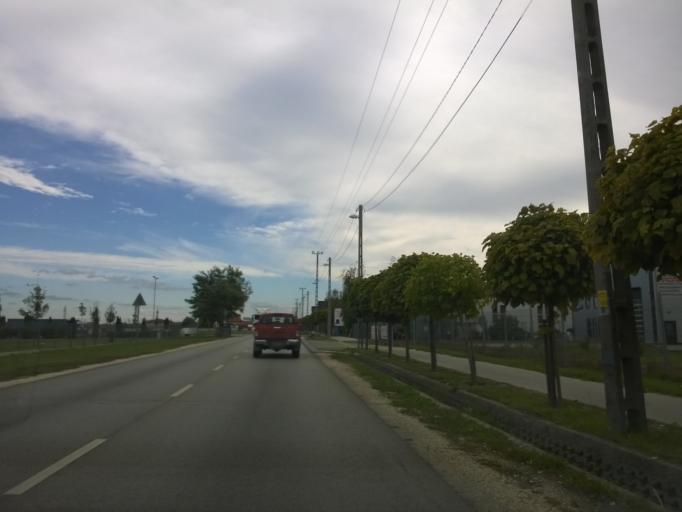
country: HU
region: Pest
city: Szigetszentmiklos
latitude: 47.3629
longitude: 19.0243
